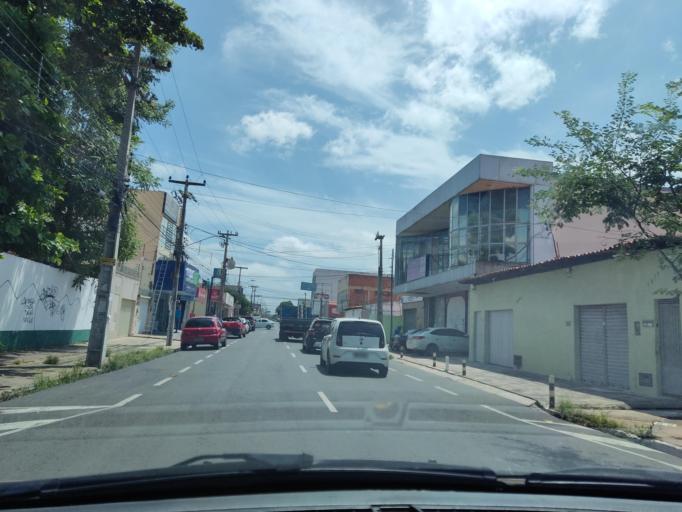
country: BR
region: Piaui
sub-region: Teresina
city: Teresina
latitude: -5.0848
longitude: -42.8167
